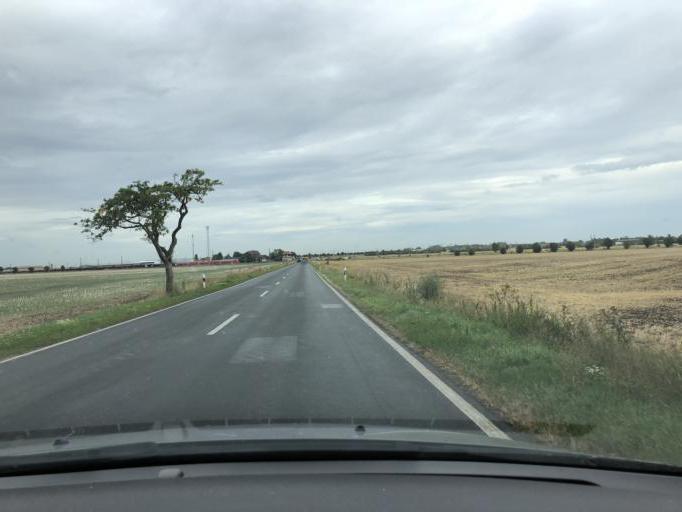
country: DE
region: Saxony-Anhalt
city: Gross Rosenburg
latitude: 51.8664
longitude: 11.8629
